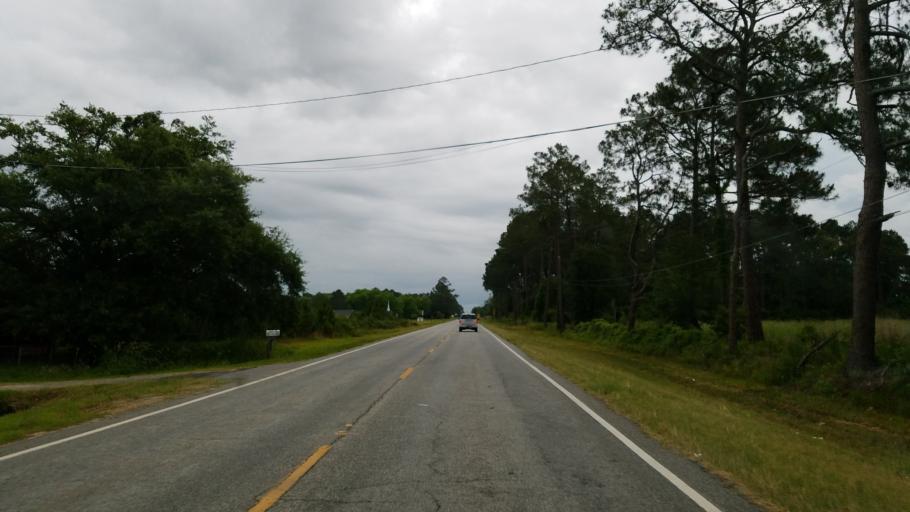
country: US
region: Georgia
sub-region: Berrien County
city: Ray City
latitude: 31.0690
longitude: -83.1753
